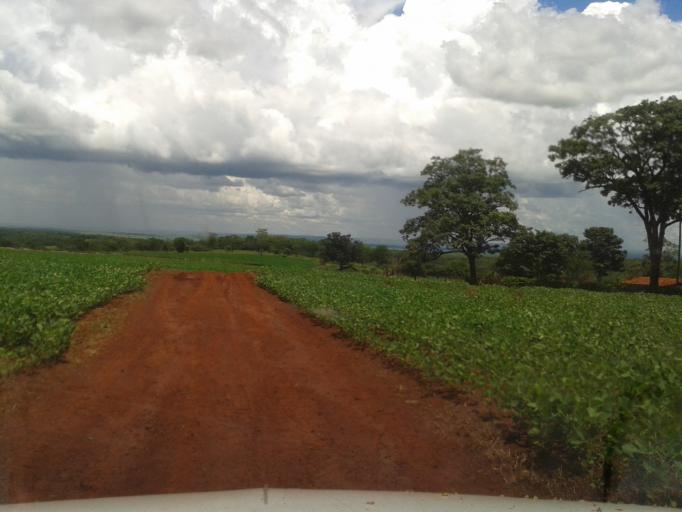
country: BR
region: Minas Gerais
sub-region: Centralina
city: Centralina
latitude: -18.6622
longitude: -49.1827
